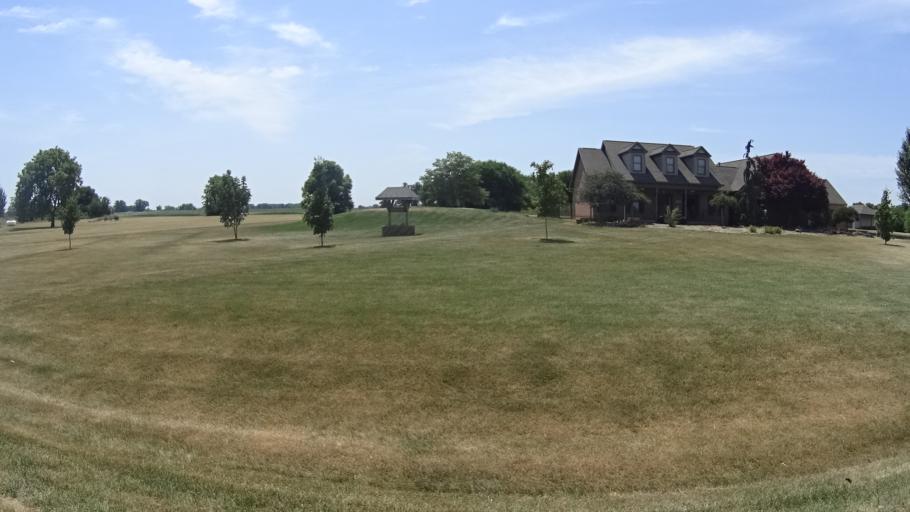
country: US
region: Ohio
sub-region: Erie County
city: Sandusky
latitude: 41.3678
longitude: -82.7633
